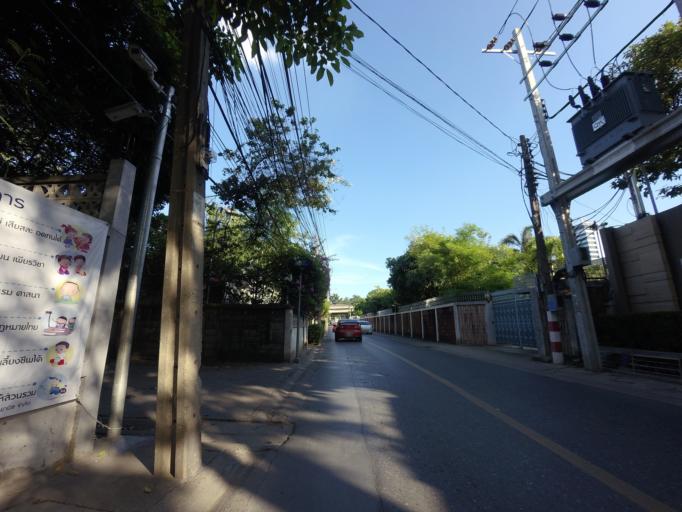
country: TH
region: Bangkok
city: Watthana
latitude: 13.7458
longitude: 100.5901
